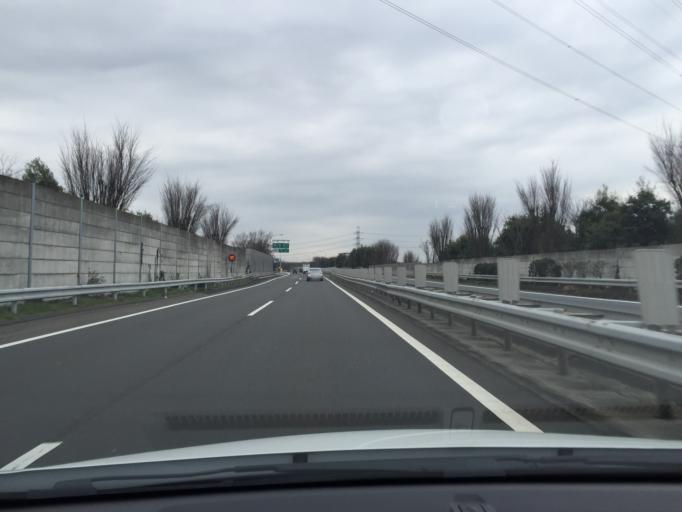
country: JP
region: Saitama
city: Sakado
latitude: 35.9236
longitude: 139.3914
